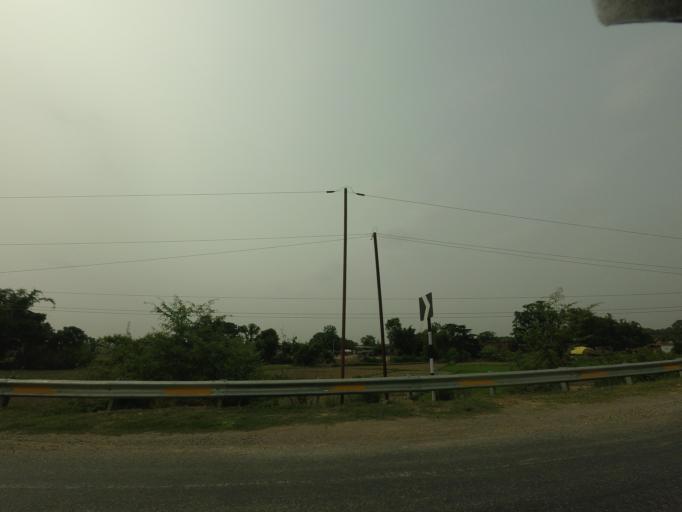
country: IN
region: Uttar Pradesh
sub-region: Maharajganj
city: Nautanwa
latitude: 27.4997
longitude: 83.3359
